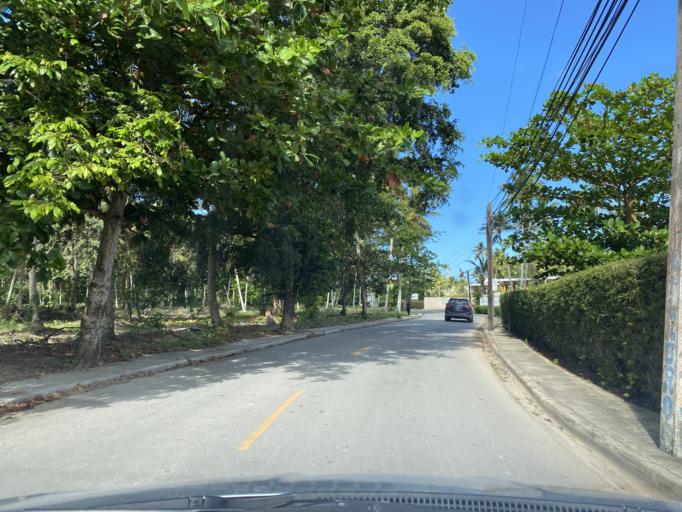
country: DO
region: Samana
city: Las Terrenas
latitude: 19.3111
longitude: -69.5646
